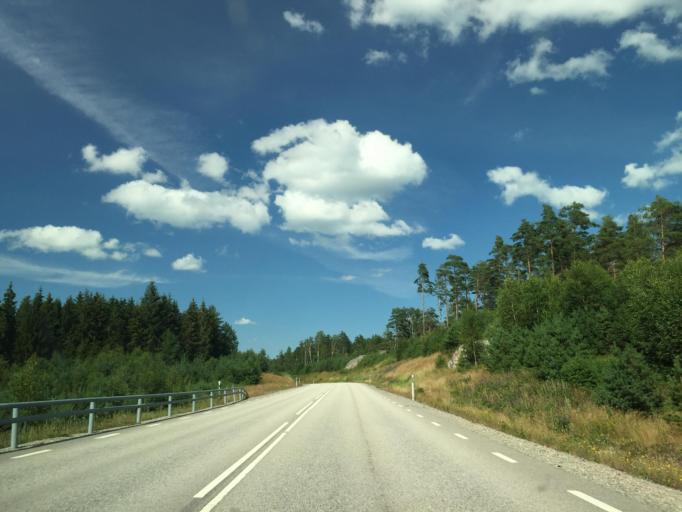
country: SE
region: Vaestra Goetaland
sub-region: Tanums Kommun
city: Tanumshede
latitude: 58.7398
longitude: 11.2935
